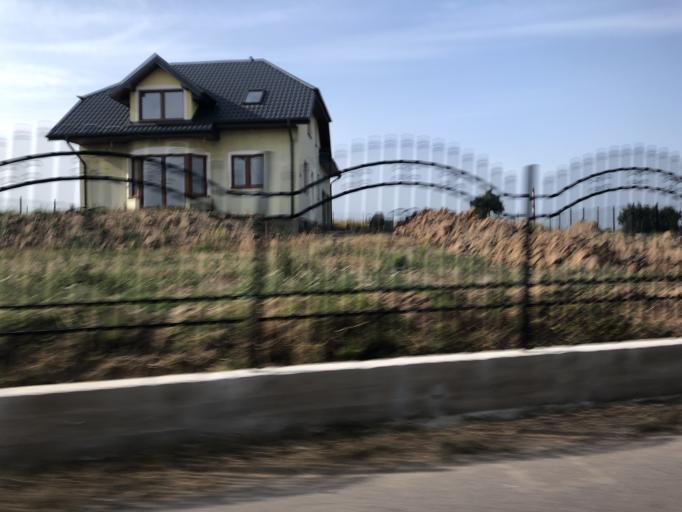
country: PL
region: Podlasie
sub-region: Lomza
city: Lomza
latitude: 53.1549
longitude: 22.0248
